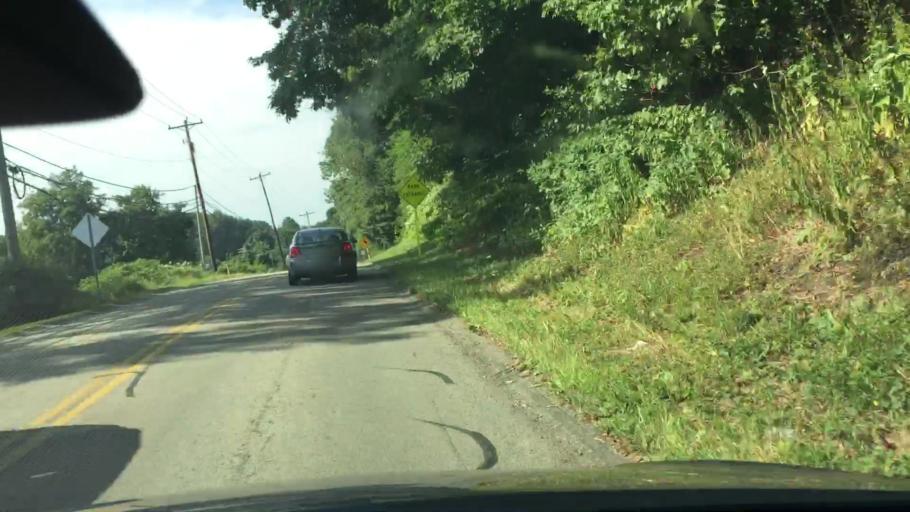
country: US
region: Pennsylvania
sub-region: Allegheny County
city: Pitcairn
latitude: 40.4226
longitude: -79.7615
